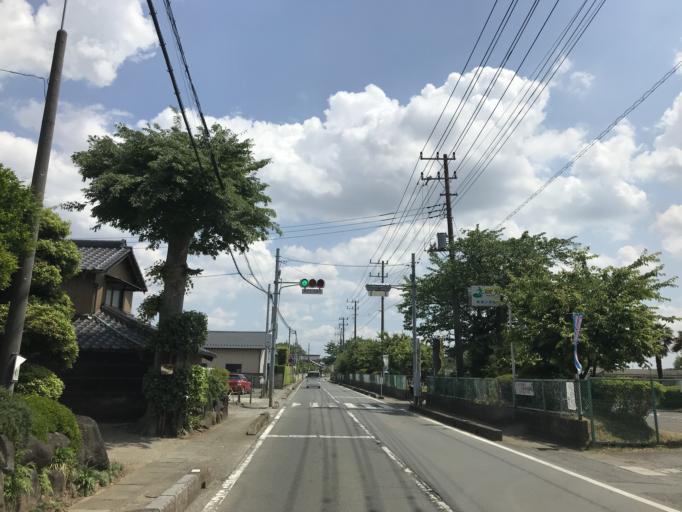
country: JP
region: Ibaraki
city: Mitsukaido
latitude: 36.0587
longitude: 140.0355
